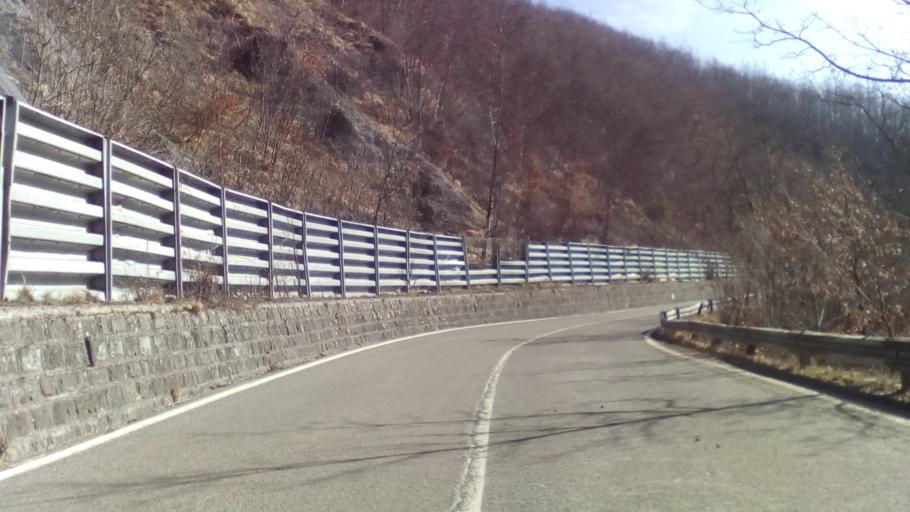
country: IT
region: Emilia-Romagna
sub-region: Provincia di Modena
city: Pievepelago
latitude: 44.2191
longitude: 10.6148
